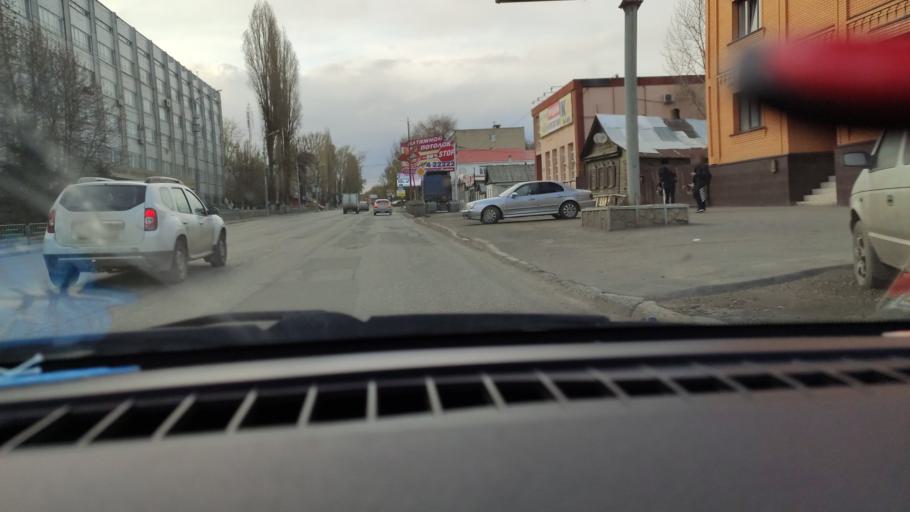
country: RU
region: Saratov
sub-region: Saratovskiy Rayon
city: Saratov
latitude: 51.5527
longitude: 46.0094
